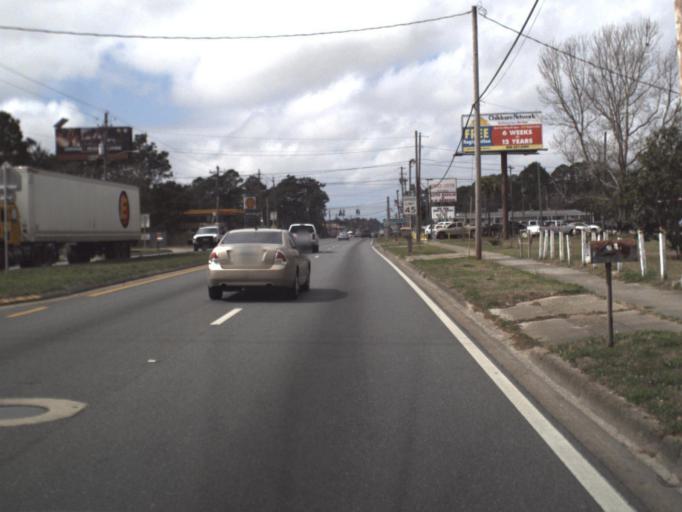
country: US
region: Florida
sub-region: Bay County
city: Cedar Grove
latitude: 30.1750
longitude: -85.6228
